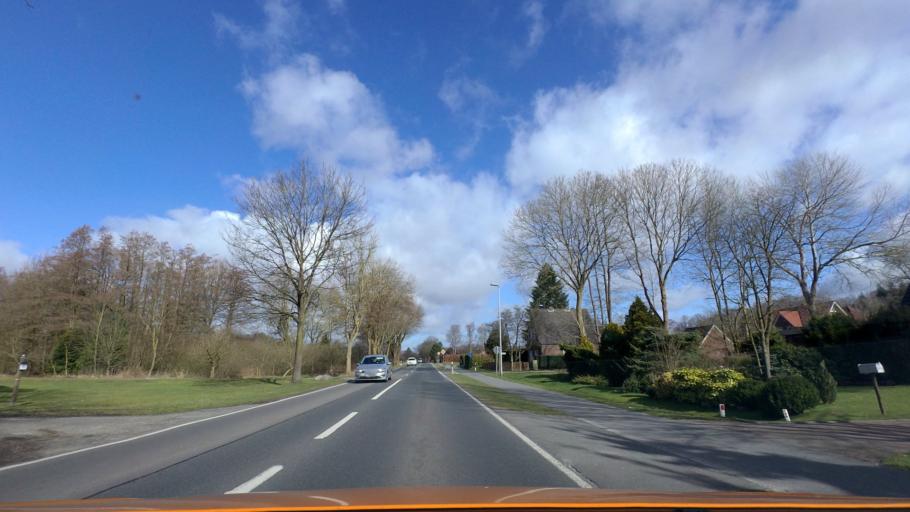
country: DE
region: Lower Saxony
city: Edewecht
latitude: 53.1472
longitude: 7.9982
